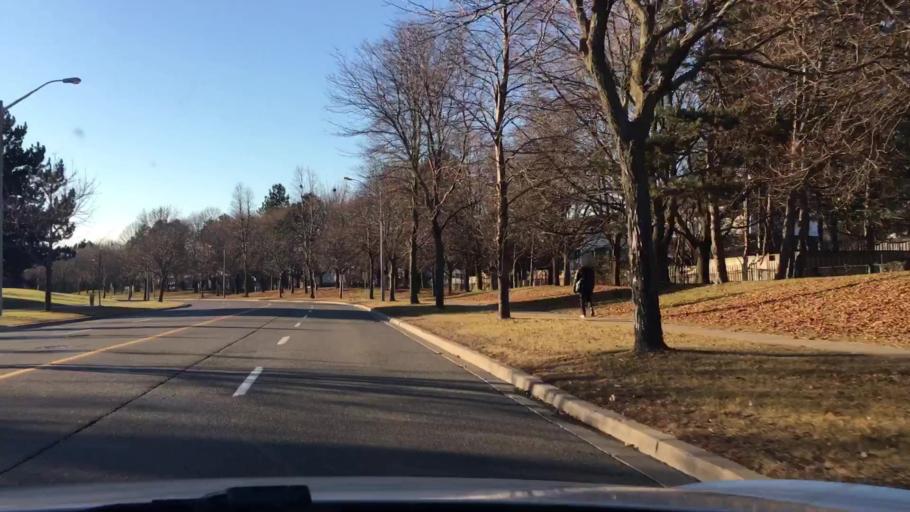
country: CA
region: Ontario
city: Scarborough
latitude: 43.7961
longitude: -79.2122
